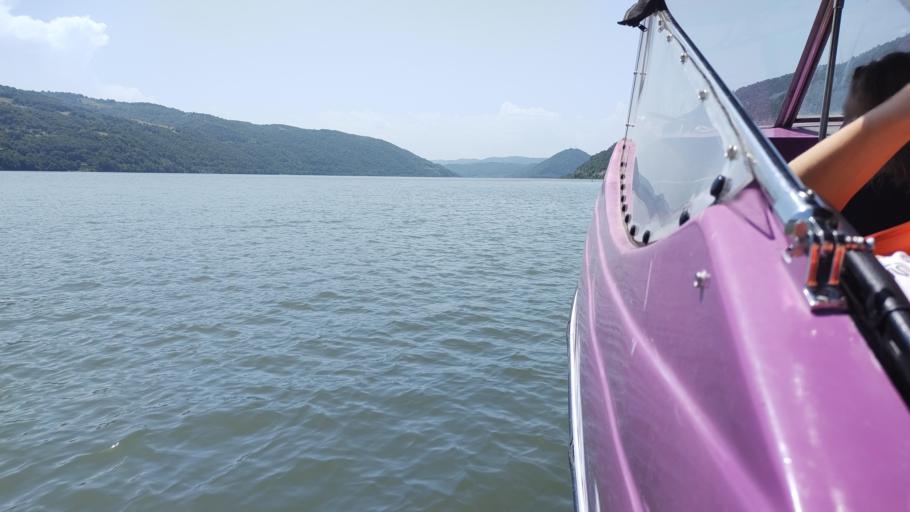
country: RO
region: Mehedinti
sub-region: Comuna Svinita
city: Svinita
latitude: 44.5074
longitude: 22.1940
